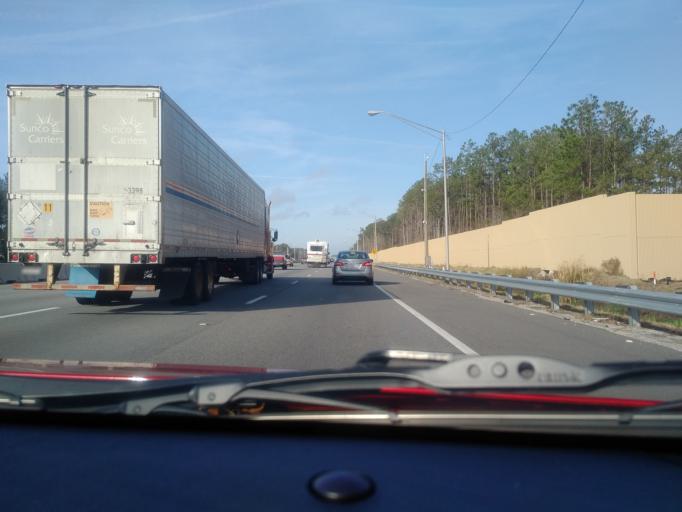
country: US
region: Florida
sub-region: Saint Johns County
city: Fruit Cove
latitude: 30.1680
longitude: -81.5775
